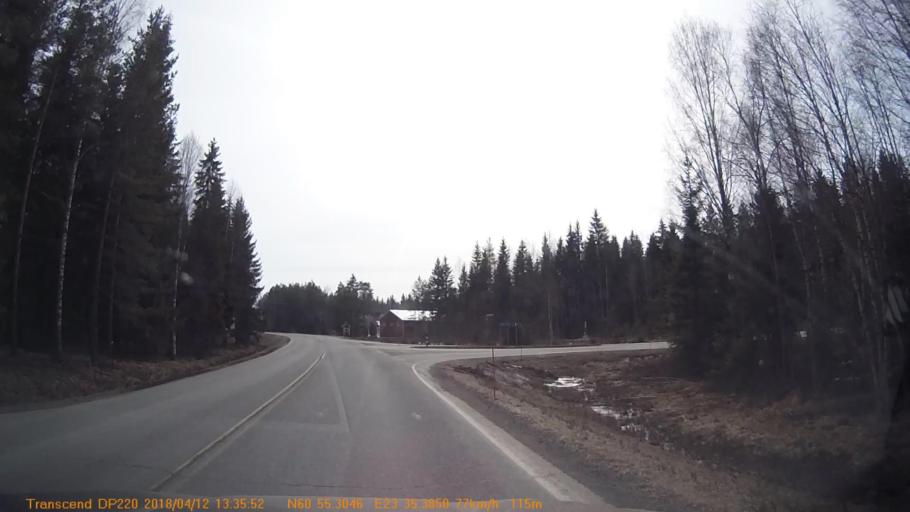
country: FI
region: Haeme
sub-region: Forssa
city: Forssa
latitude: 60.9216
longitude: 23.5897
